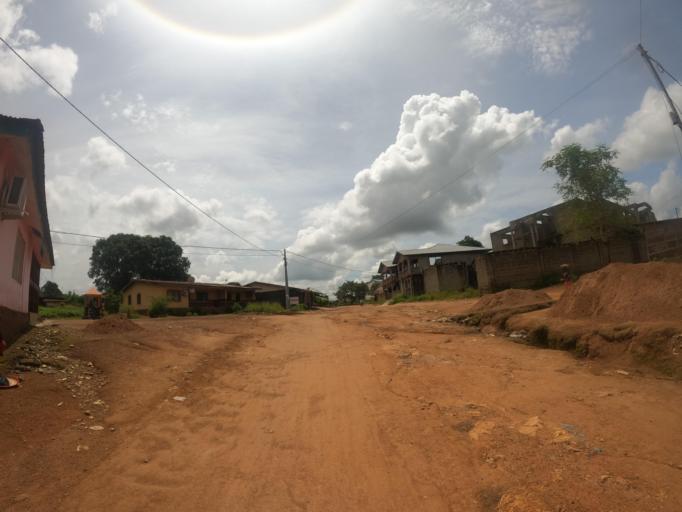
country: SL
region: Northern Province
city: Makeni
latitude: 8.8947
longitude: -12.0495
